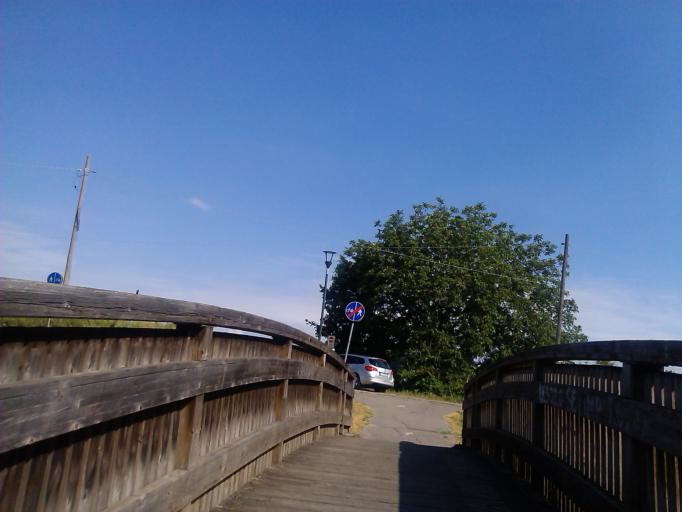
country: IT
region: Tuscany
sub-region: Provincia di Prato
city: Prato
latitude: 43.8636
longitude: 11.1189
